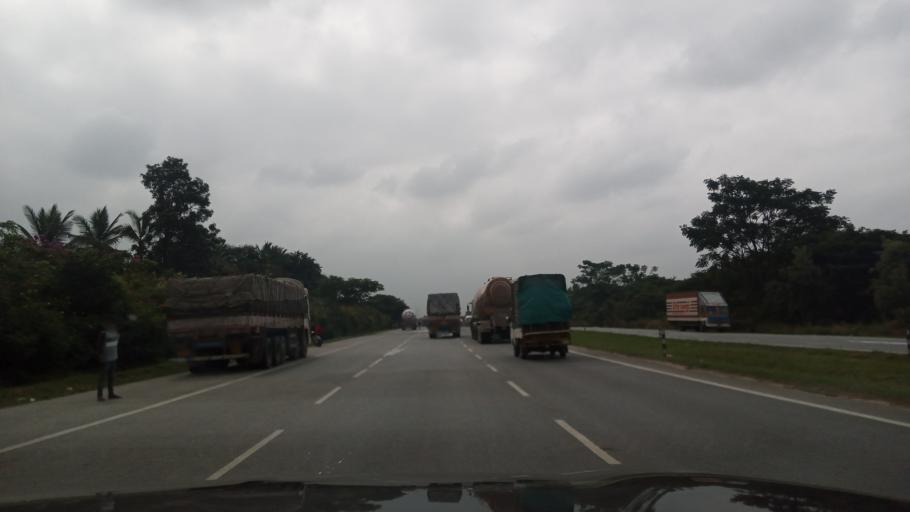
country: IN
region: Karnataka
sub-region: Bangalore Rural
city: Nelamangala
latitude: 13.0515
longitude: 77.4765
